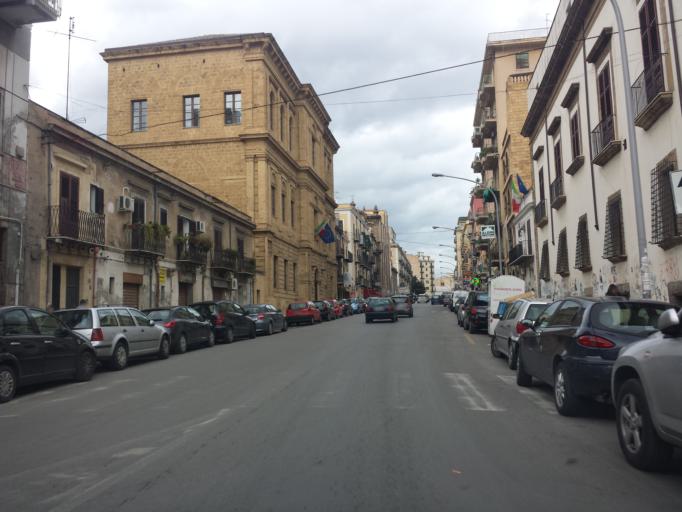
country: IT
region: Sicily
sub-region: Palermo
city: Palermo
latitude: 38.1153
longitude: 13.3533
